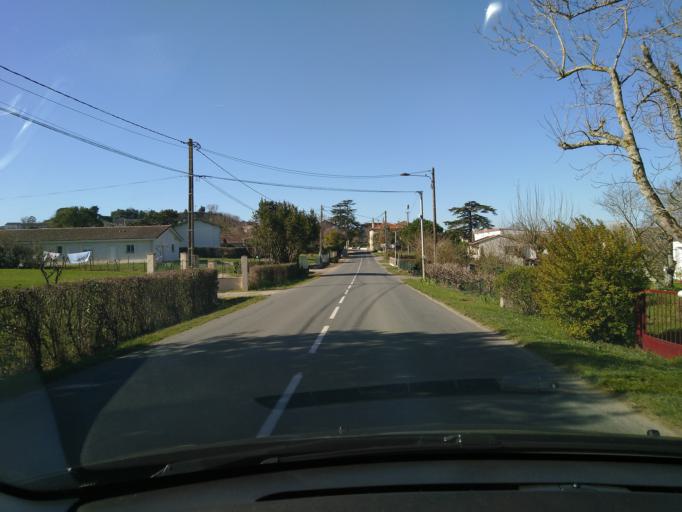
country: FR
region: Aquitaine
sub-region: Departement du Lot-et-Garonne
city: Cancon
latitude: 44.5356
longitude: 0.6312
